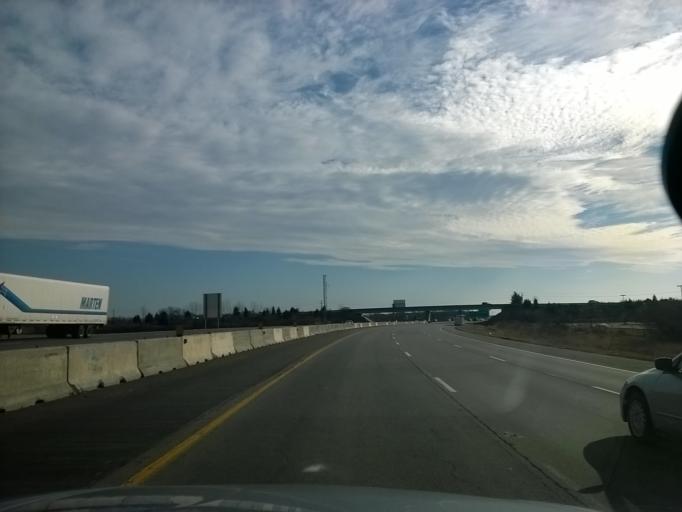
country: US
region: Indiana
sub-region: Johnson County
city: Greenwood
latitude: 39.6535
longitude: -86.0747
